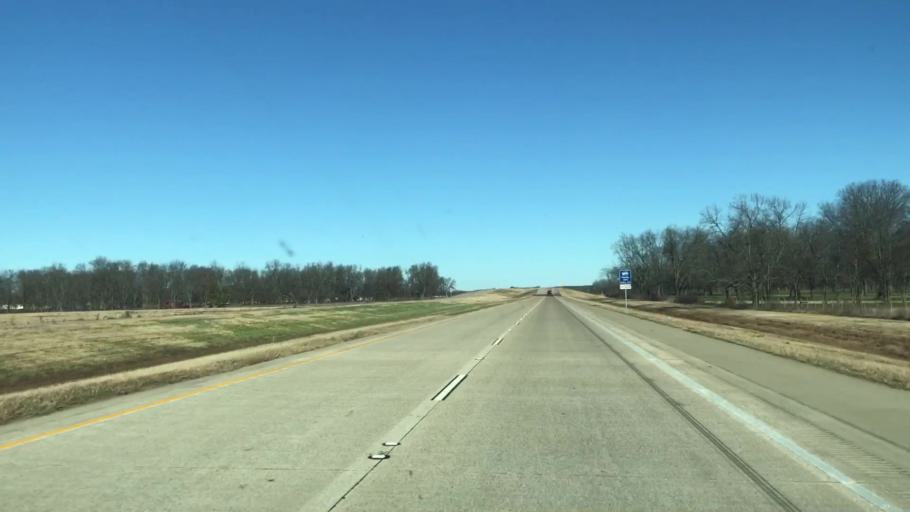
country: US
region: Louisiana
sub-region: Caddo Parish
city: Oil City
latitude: 32.7398
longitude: -93.8771
